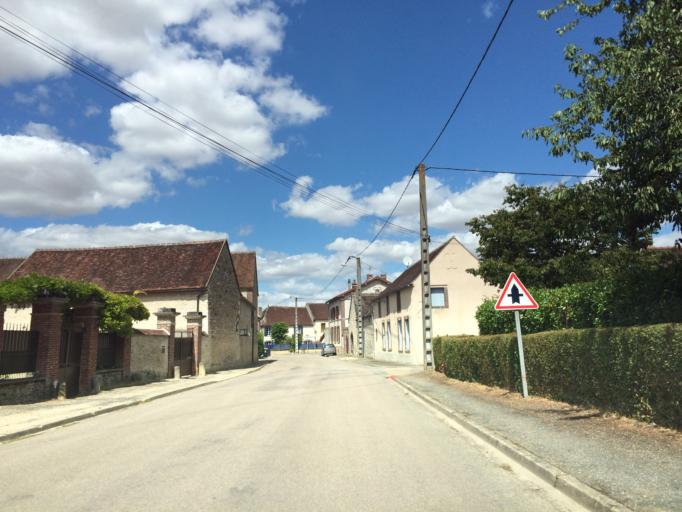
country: FR
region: Bourgogne
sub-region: Departement de l'Yonne
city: Fleury-la-Vallee
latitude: 47.8856
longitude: 3.4820
